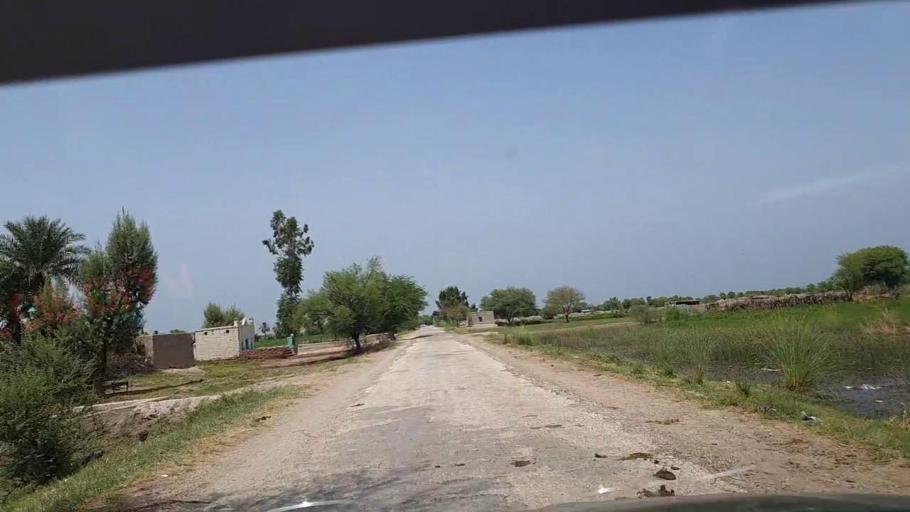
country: PK
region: Sindh
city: Khanpur
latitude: 27.8056
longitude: 69.4506
